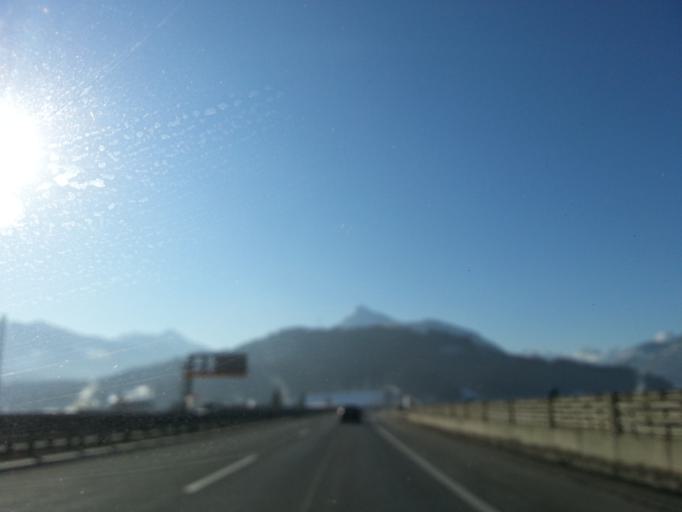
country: AT
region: Salzburg
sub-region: Politischer Bezirk Sankt Johann im Pongau
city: Eben im Pongau
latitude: 47.3872
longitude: 13.4007
